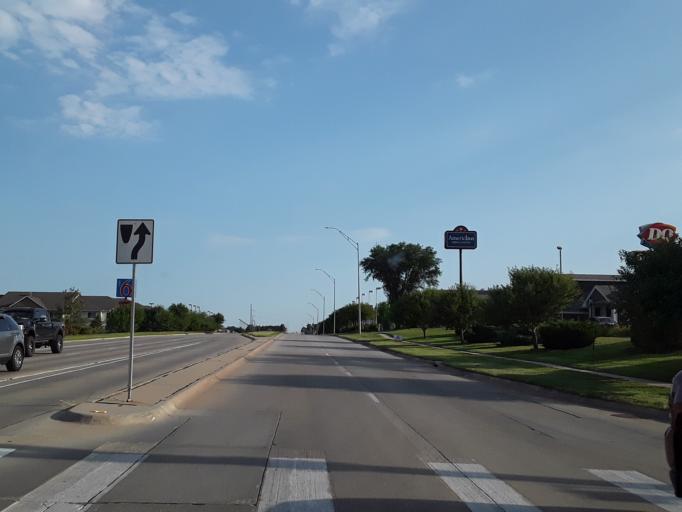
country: US
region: Nebraska
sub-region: Lancaster County
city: Lincoln
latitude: 40.8788
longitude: -96.6820
